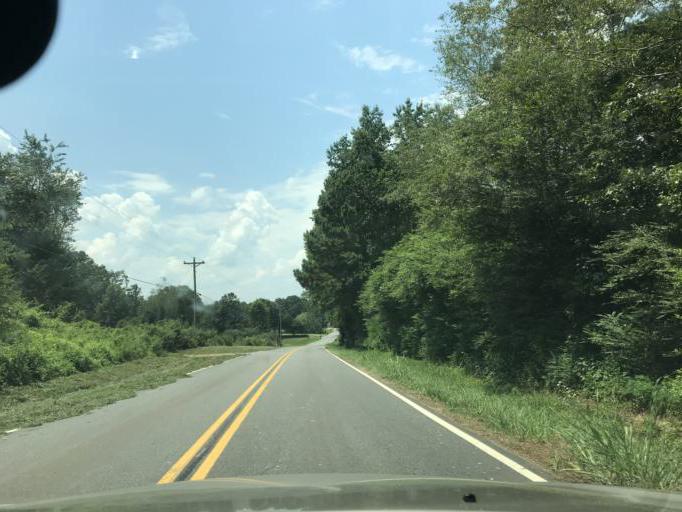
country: US
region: Georgia
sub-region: Dawson County
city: Dawsonville
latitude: 34.3222
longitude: -84.1641
